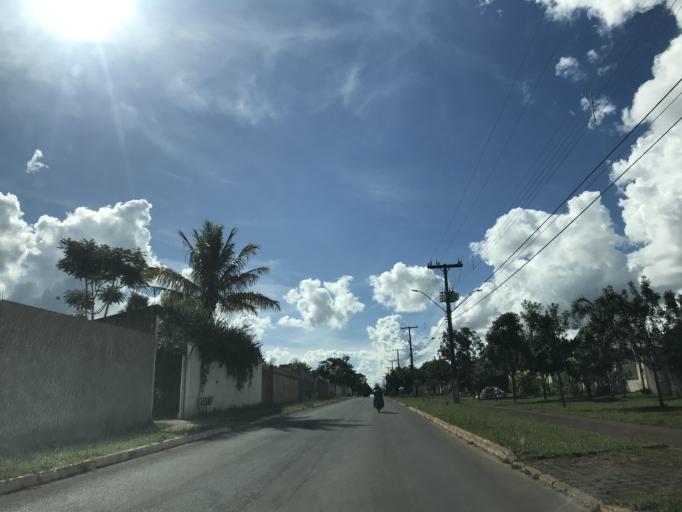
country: BR
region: Federal District
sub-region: Brasilia
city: Brasilia
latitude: -15.7474
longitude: -47.7510
